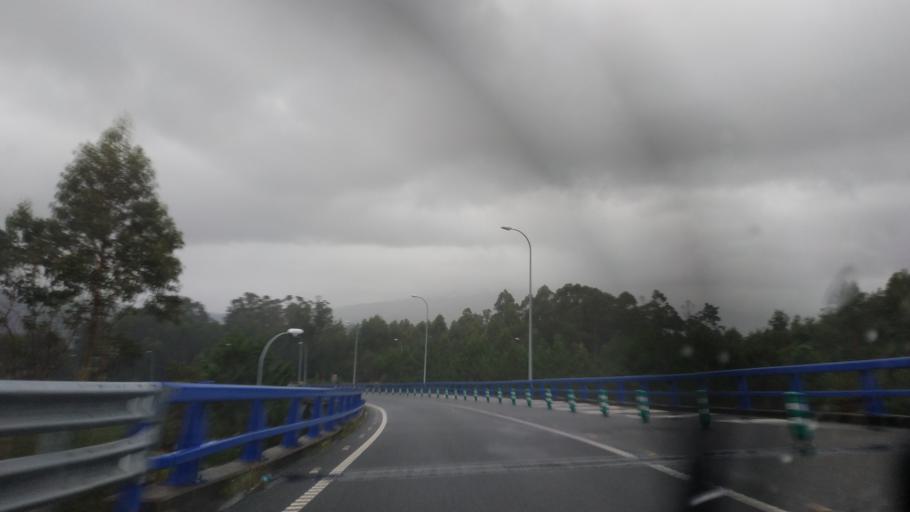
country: ES
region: Galicia
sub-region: Provincia da Coruna
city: Culleredo
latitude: 43.2740
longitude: -8.4025
